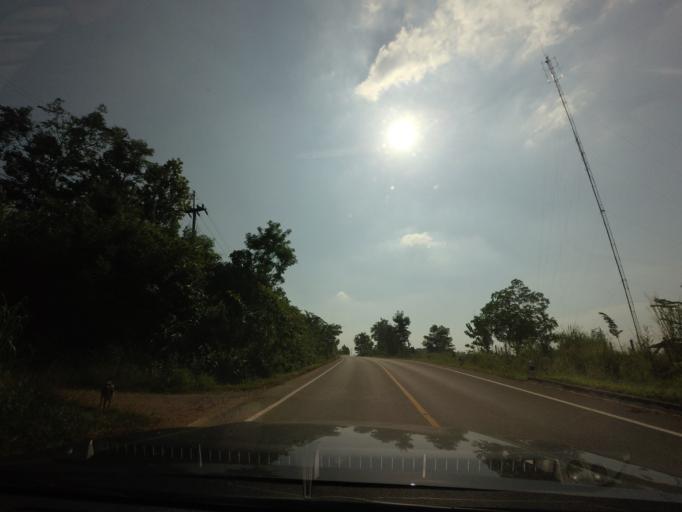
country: TH
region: Nan
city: Santi Suk
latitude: 18.9095
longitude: 100.8686
